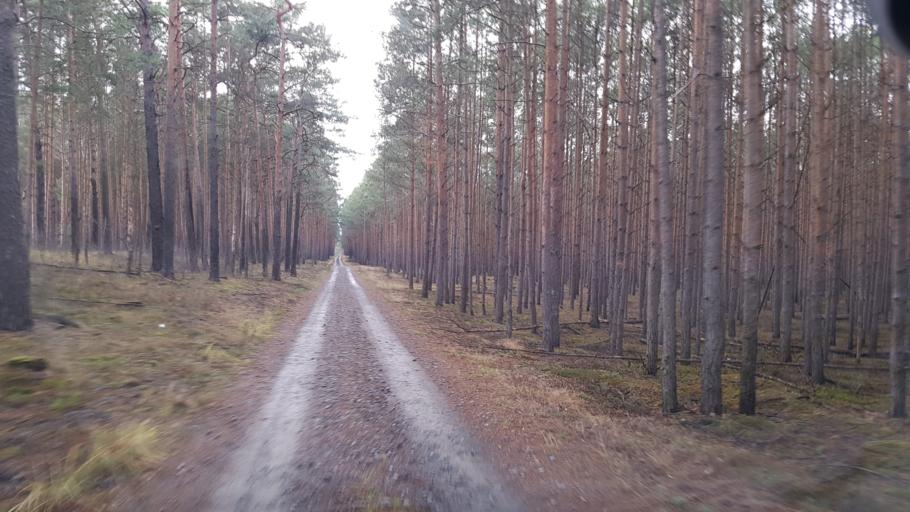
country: DE
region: Brandenburg
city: Sallgast
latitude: 51.6252
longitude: 13.8168
